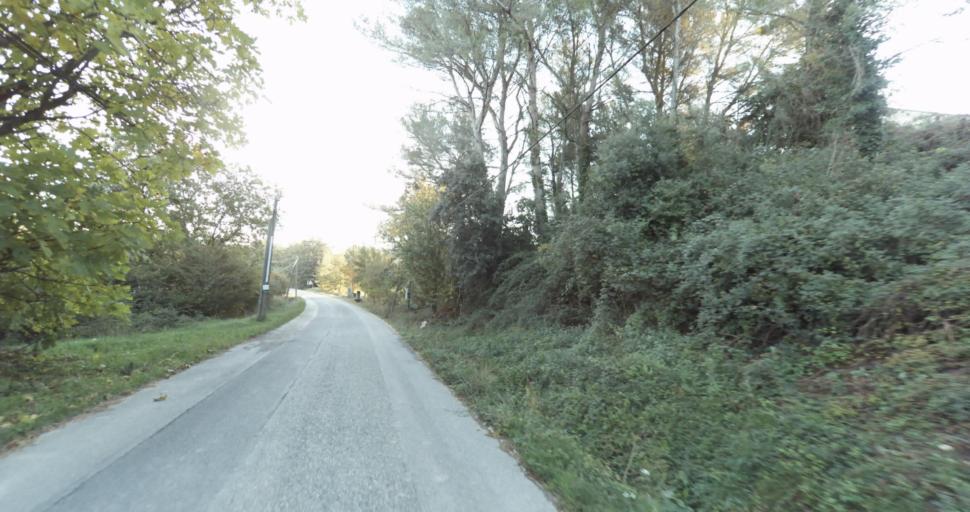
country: FR
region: Provence-Alpes-Cote d'Azur
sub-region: Departement des Bouches-du-Rhone
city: Venelles
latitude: 43.5774
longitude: 5.4953
